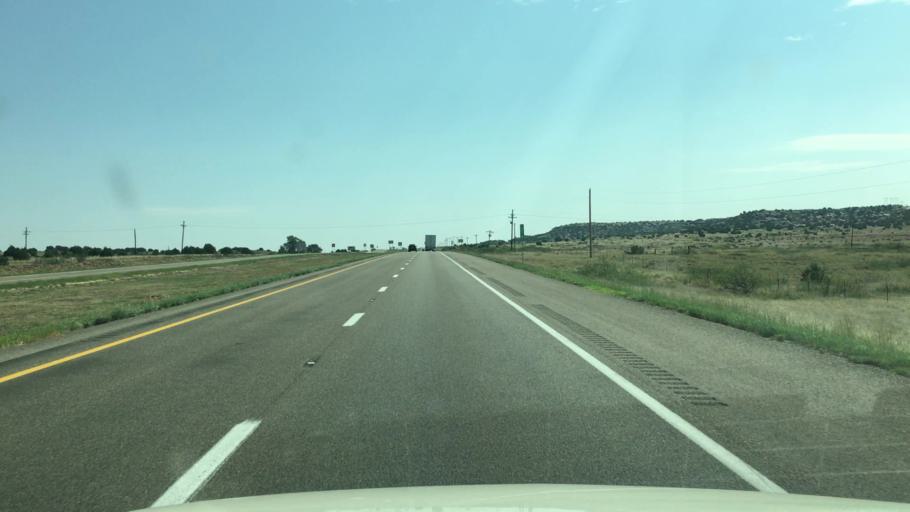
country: US
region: New Mexico
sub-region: Guadalupe County
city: Santa Rosa
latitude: 34.9540
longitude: -104.6262
